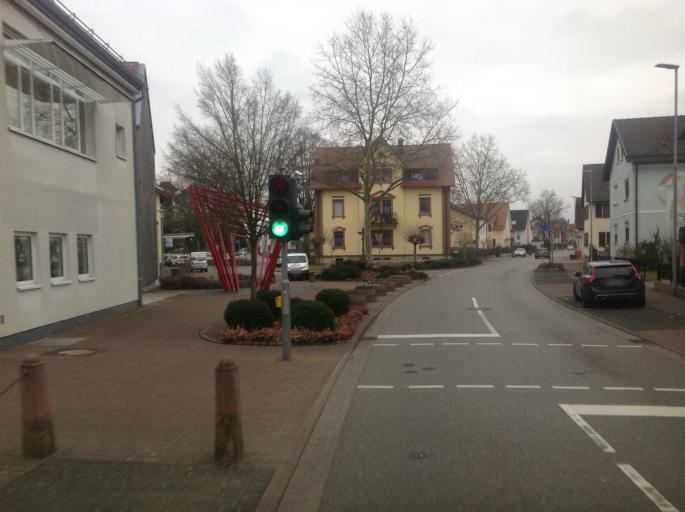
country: DE
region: Baden-Wuerttemberg
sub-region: Karlsruhe Region
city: Iffezheim
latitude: 48.8220
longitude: 8.1450
